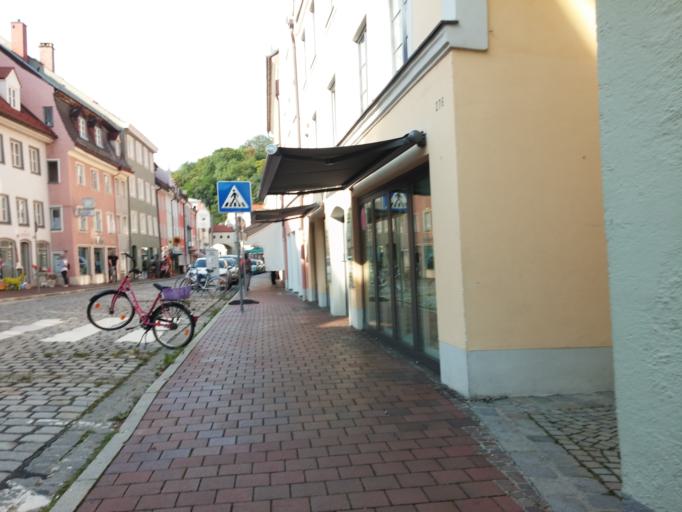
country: DE
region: Bavaria
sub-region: Upper Bavaria
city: Landsberg am Lech
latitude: 48.0519
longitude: 10.8767
